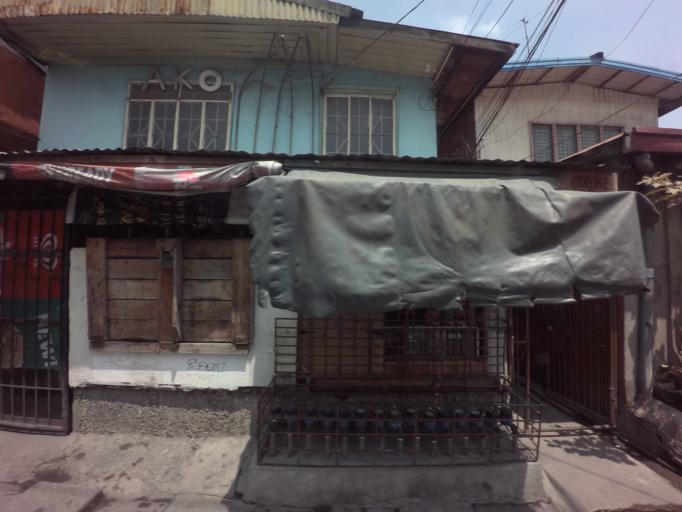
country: PH
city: Sambayanihan People's Village
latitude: 14.4416
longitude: 121.0506
